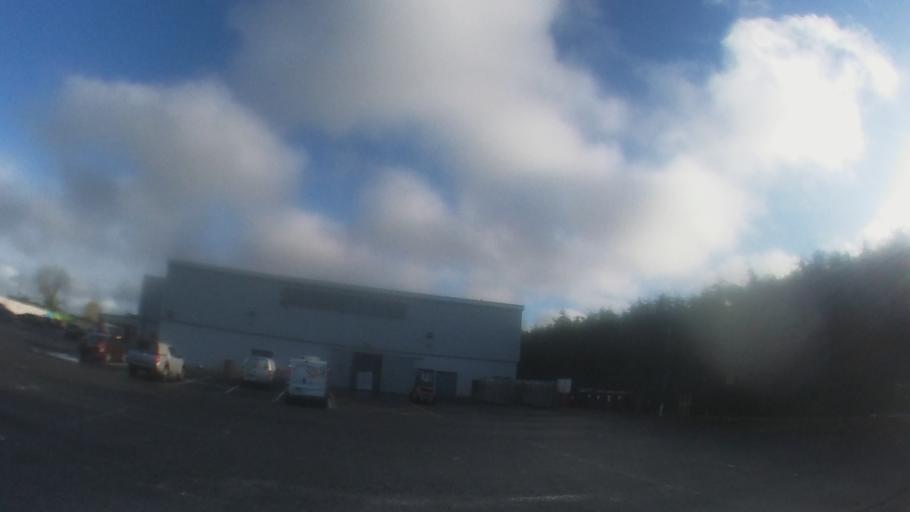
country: IE
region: Connaught
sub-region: Roscommon
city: Ballaghaderreen
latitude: 53.9025
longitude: -8.5854
